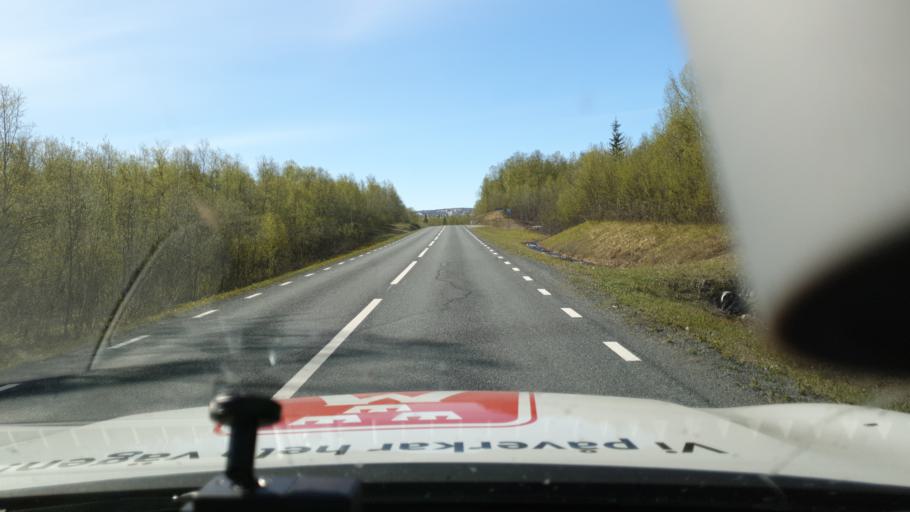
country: NO
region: Nordland
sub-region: Rana
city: Mo i Rana
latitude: 65.7655
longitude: 15.1143
